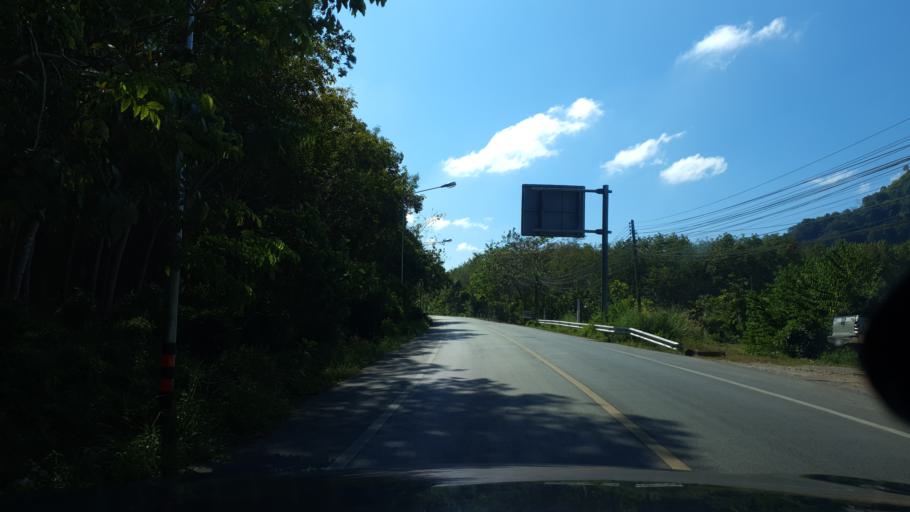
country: TH
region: Phangnga
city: Ban Ao Nang
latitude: 8.0761
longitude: 98.8053
